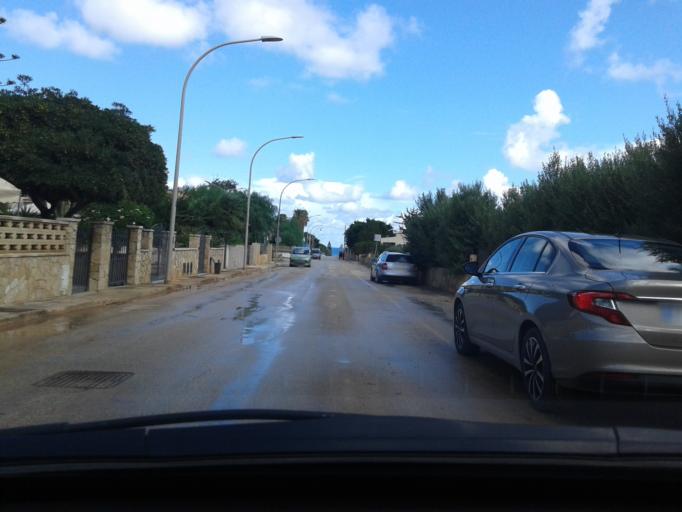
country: IT
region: Sicily
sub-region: Trapani
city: San Vito Lo Capo
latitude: 38.1697
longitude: 12.7422
